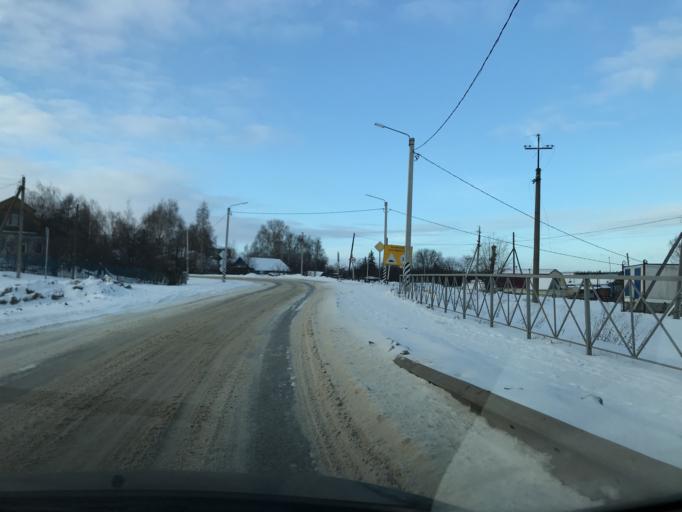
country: RU
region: Ulyanovsk
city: Undory
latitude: 54.6090
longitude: 48.3909
